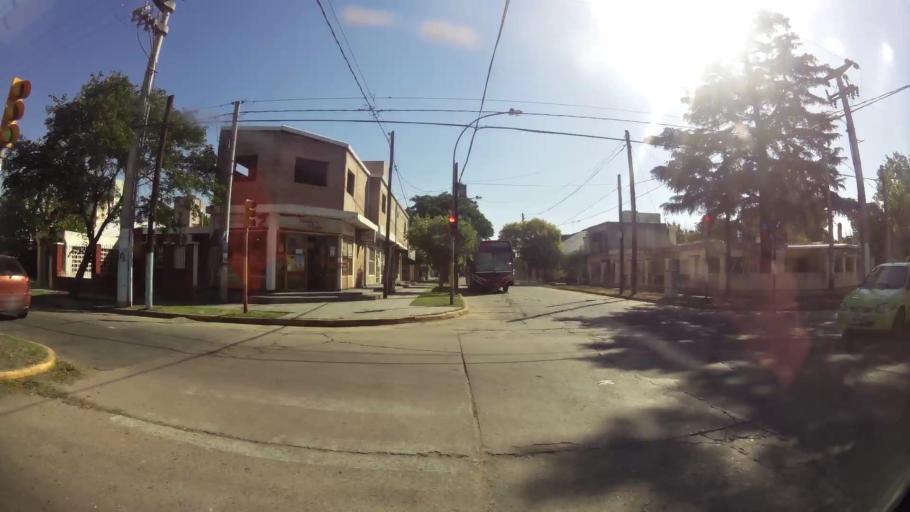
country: AR
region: Cordoba
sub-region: Departamento de Capital
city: Cordoba
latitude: -31.3671
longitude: -64.1994
